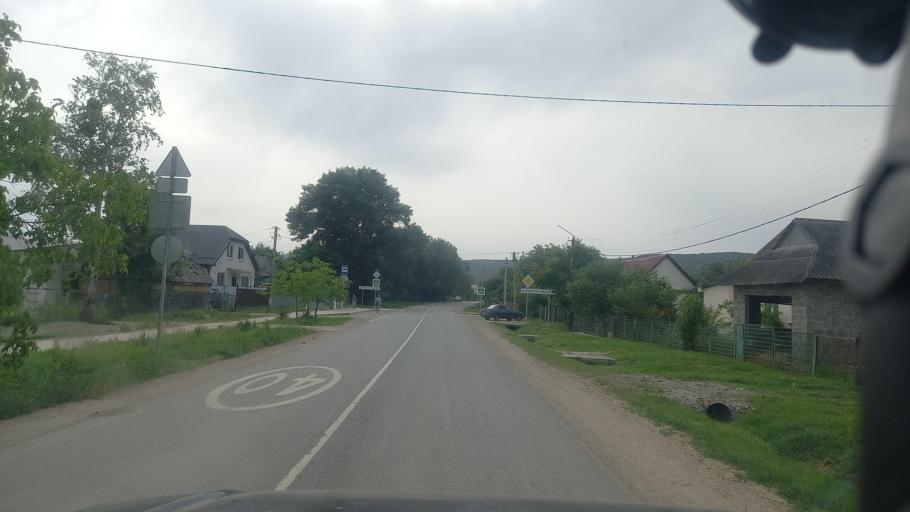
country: RU
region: Krasnodarskiy
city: Goryachiy Klyuch
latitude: 44.6073
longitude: 39.0321
